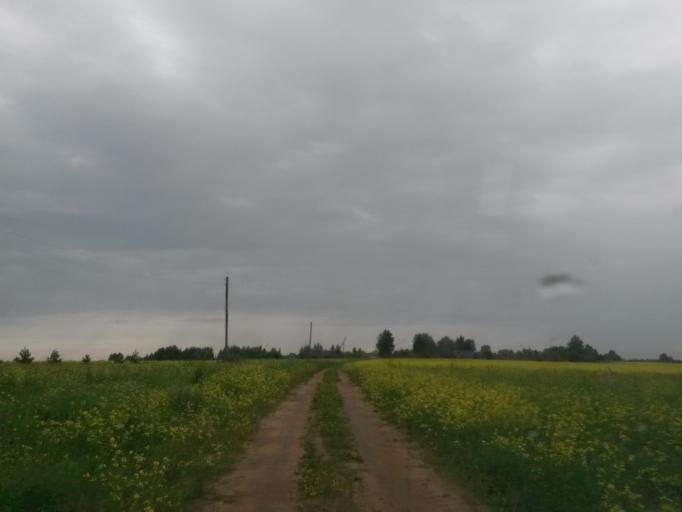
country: RU
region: Jaroslavl
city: Tutayev
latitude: 57.9419
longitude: 39.4407
